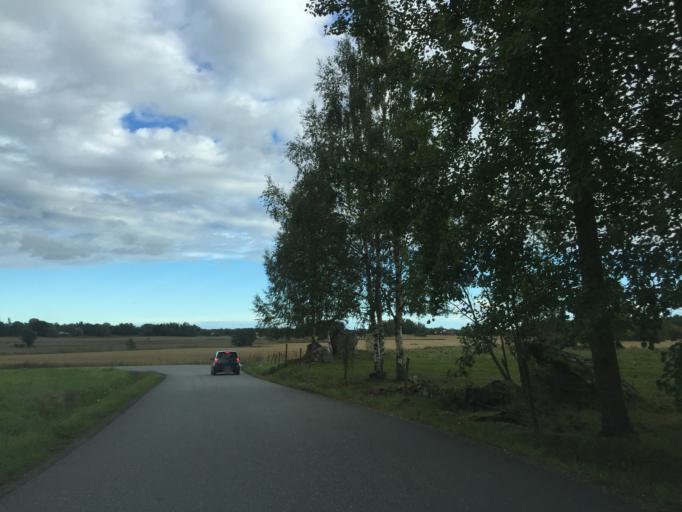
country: SE
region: OErebro
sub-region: Orebro Kommun
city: Hovsta
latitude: 59.3210
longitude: 15.1940
